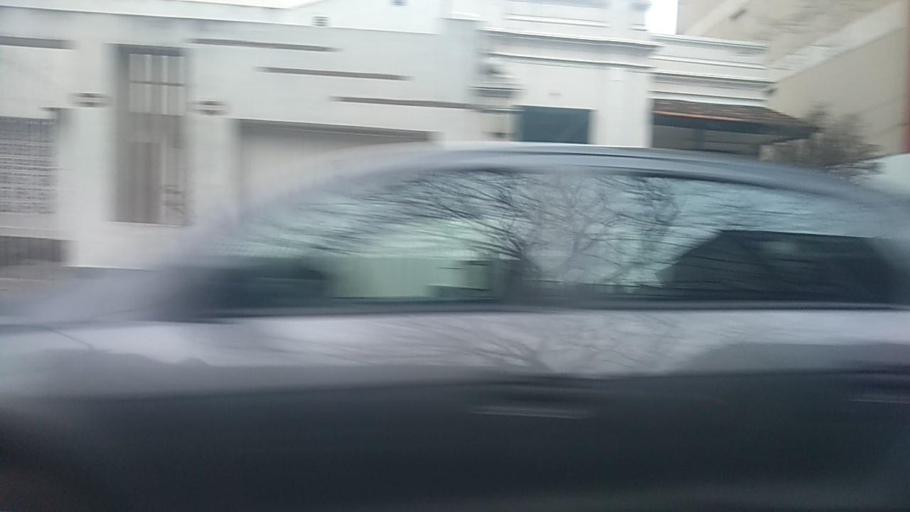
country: AR
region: Buenos Aires F.D.
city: Villa Santa Rita
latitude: -34.5986
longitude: -58.4992
